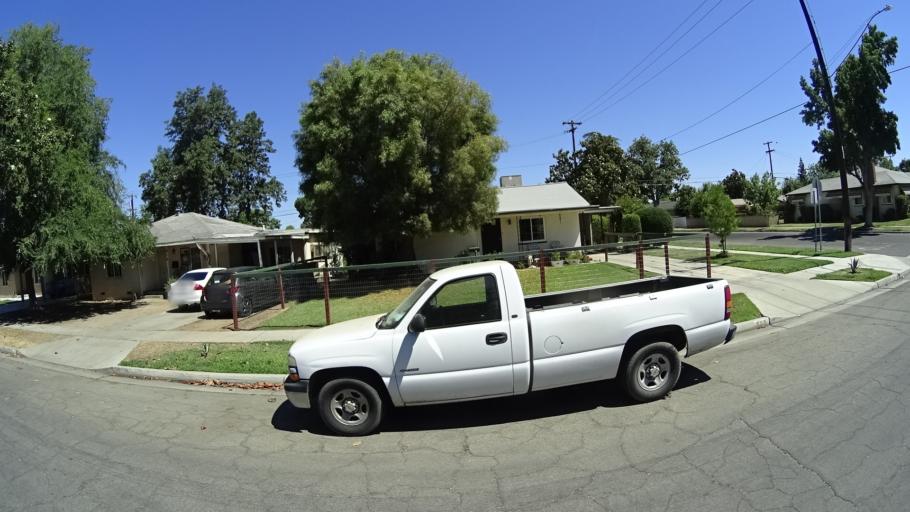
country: US
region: California
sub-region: Fresno County
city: Fresno
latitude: 36.7821
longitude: -119.8223
